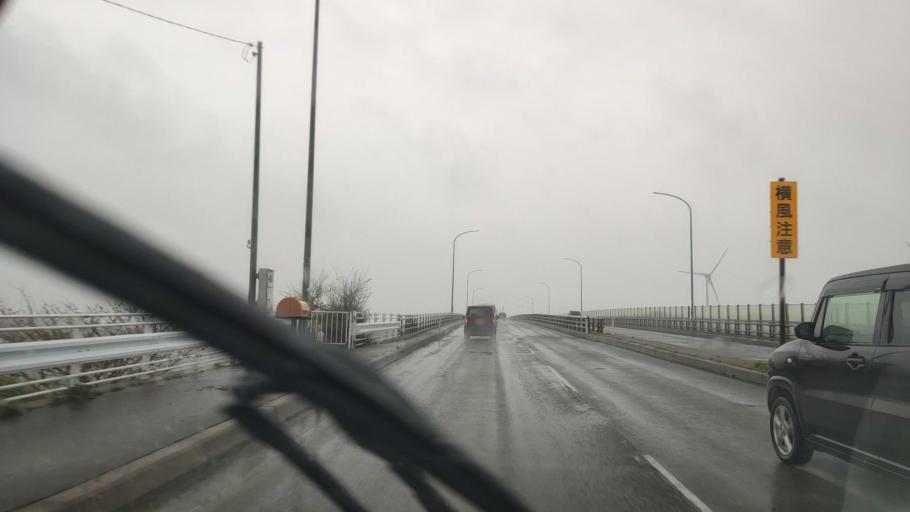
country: JP
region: Akita
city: Tenno
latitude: 39.8970
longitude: 139.9493
